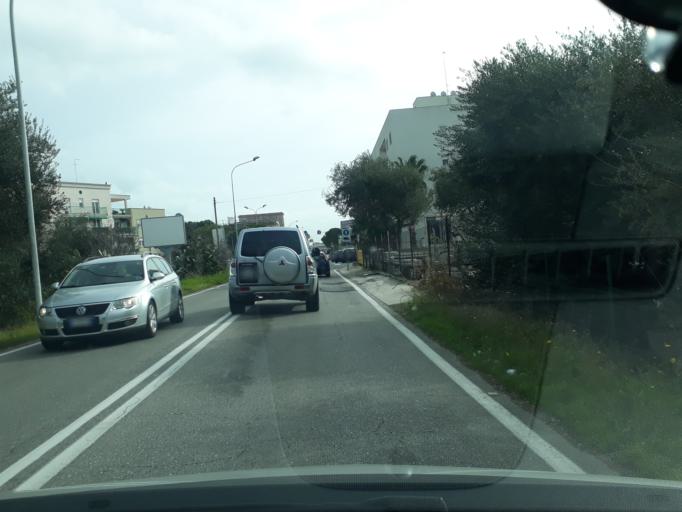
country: IT
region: Apulia
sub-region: Provincia di Bari
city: Monopoli
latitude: 40.9516
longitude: 17.2867
